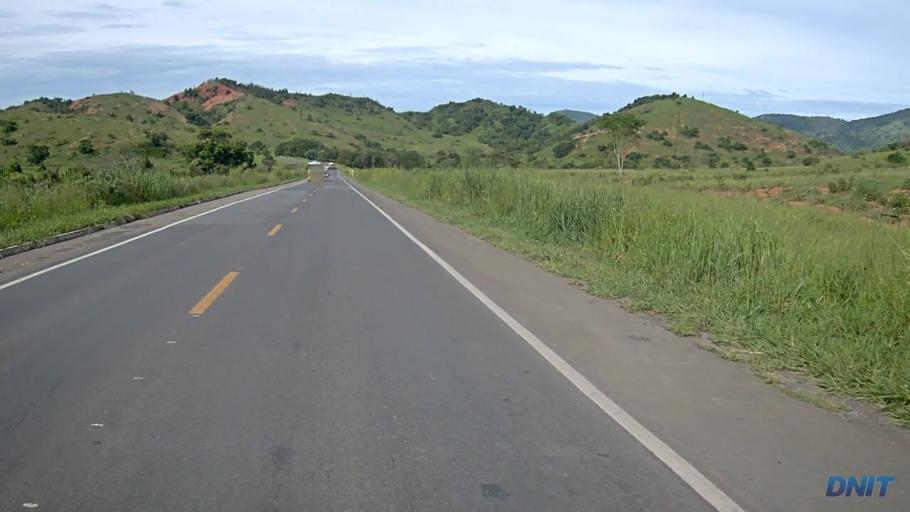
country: BR
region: Minas Gerais
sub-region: Belo Oriente
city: Belo Oriente
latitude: -19.2204
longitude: -42.3110
